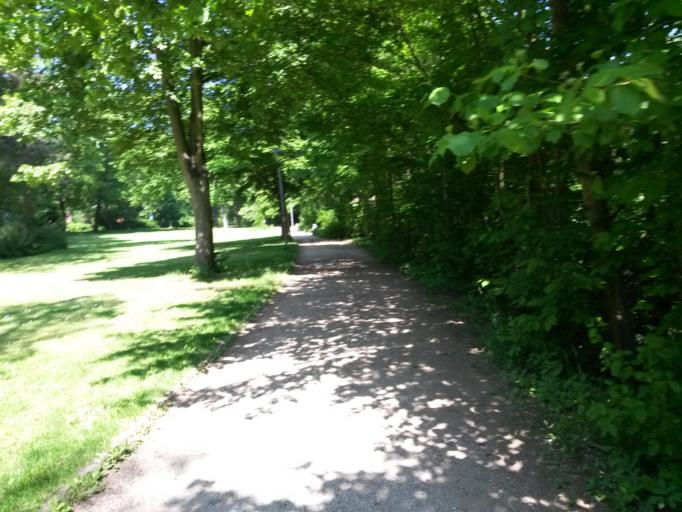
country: DE
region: Bavaria
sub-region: Regierungsbezirk Mittelfranken
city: Furth
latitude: 49.4720
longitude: 11.0048
